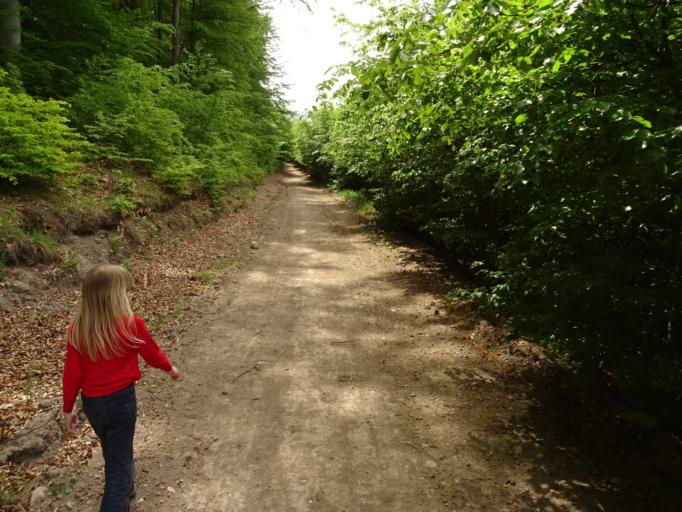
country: SK
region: Nitriansky
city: Sahy
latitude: 47.9879
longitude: 18.9552
